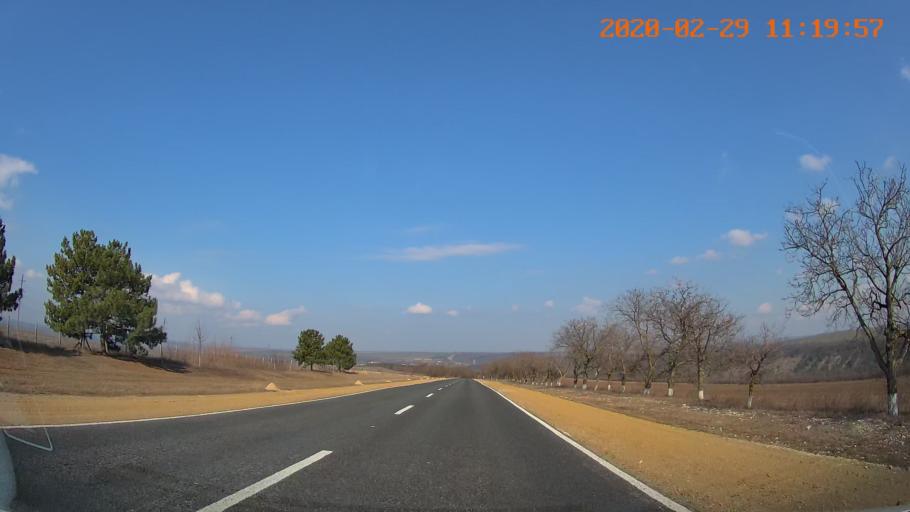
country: MD
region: Telenesti
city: Cocieri
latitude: 47.3580
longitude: 29.1728
